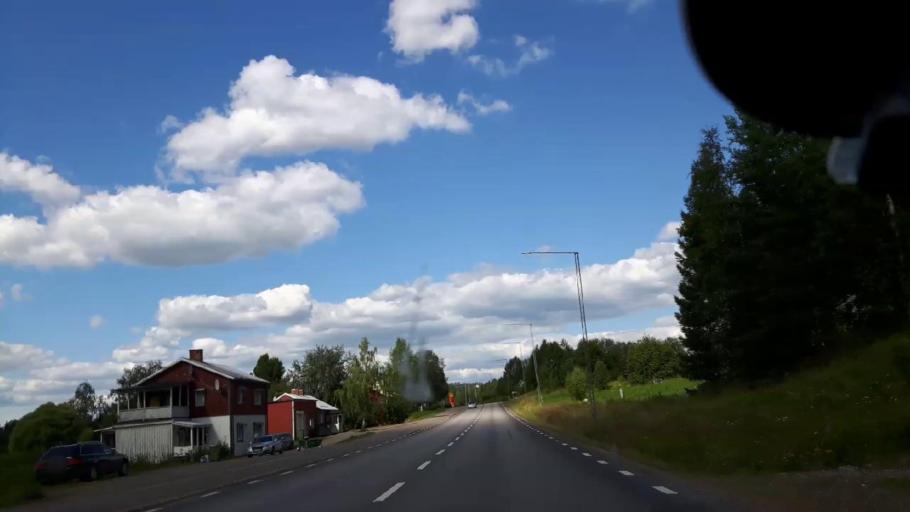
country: SE
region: Jaemtland
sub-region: Ragunda Kommun
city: Hammarstrand
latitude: 63.0073
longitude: 16.6659
